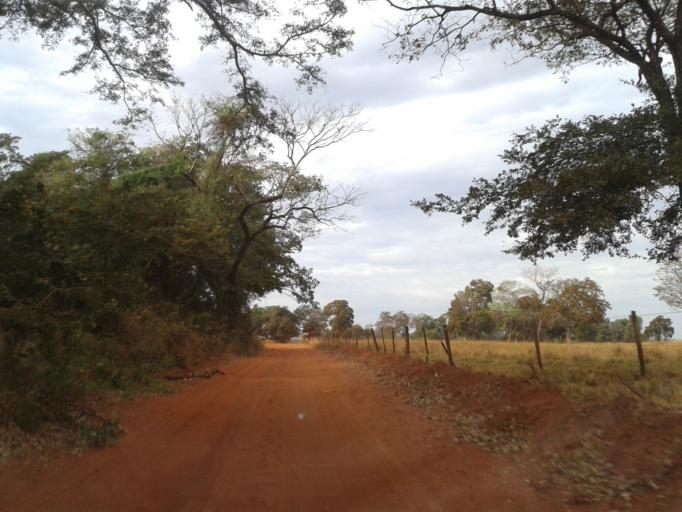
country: BR
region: Minas Gerais
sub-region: Santa Vitoria
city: Santa Vitoria
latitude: -18.7768
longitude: -50.1858
